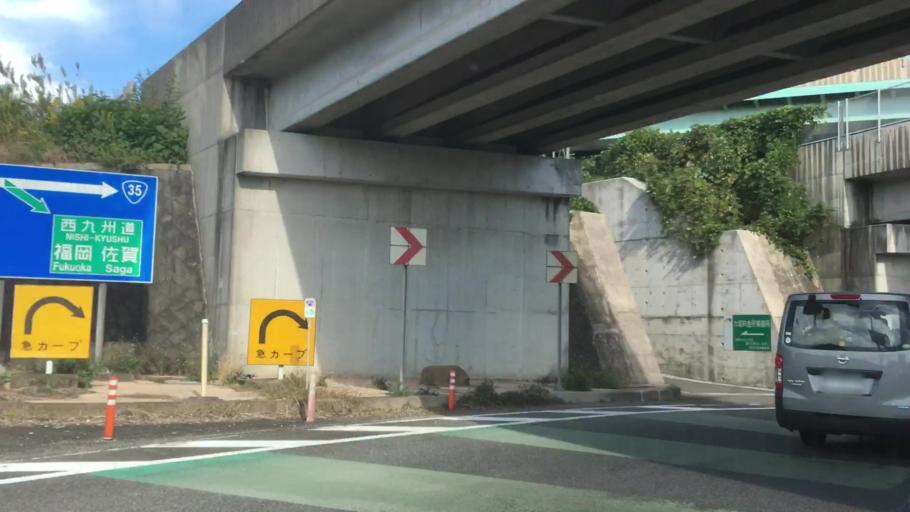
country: JP
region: Nagasaki
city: Sasebo
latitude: 33.1462
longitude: 129.7775
